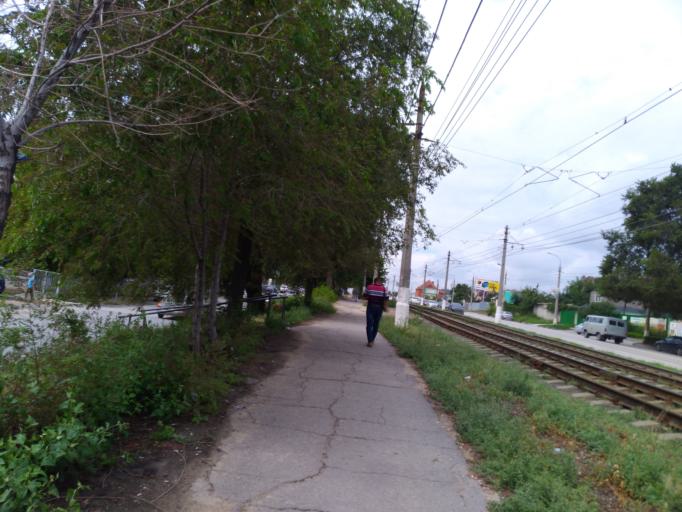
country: RU
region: Volgograd
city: Volgograd
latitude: 48.7148
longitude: 44.4931
